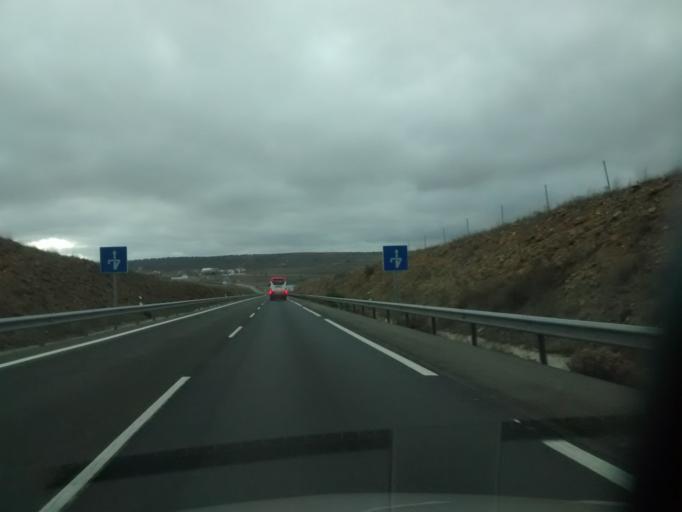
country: ES
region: Castille-La Mancha
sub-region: Provincia de Guadalajara
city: Torremocha del Campo
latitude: 40.9890
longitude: -2.6023
